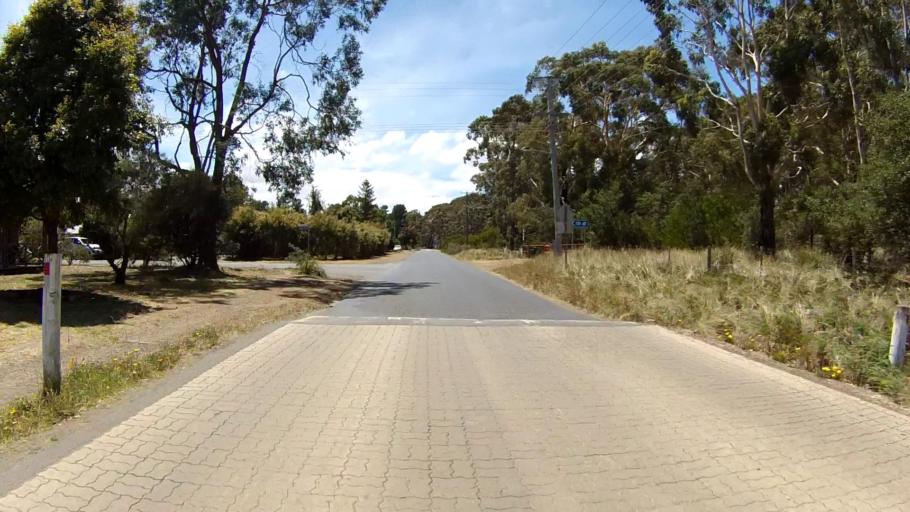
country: AU
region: Tasmania
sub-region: Clarence
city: Seven Mile Beach
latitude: -42.8574
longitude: 147.5094
